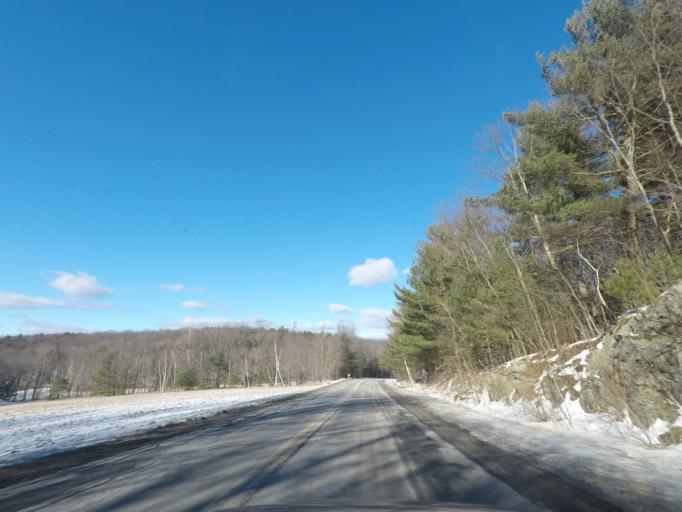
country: US
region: Massachusetts
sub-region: Berkshire County
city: Richmond
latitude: 42.3798
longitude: -73.4747
